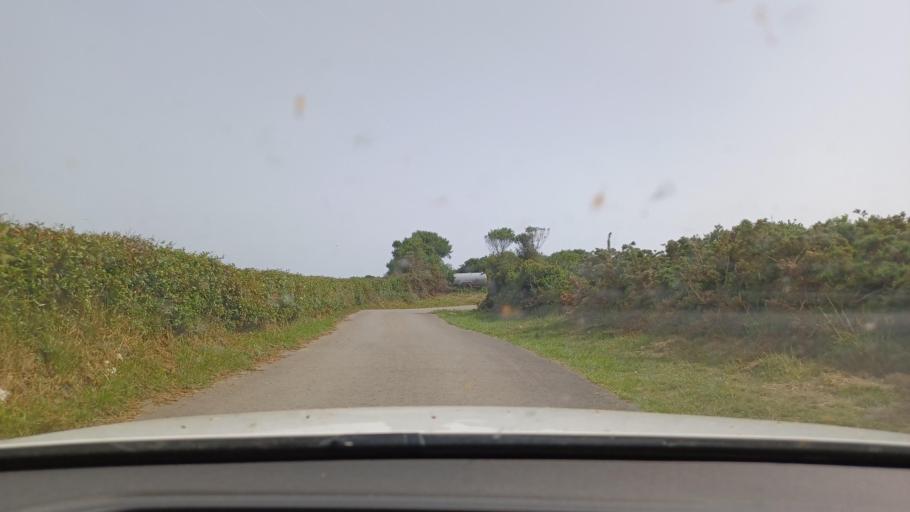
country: ES
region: Asturias
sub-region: Province of Asturias
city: Ribadesella
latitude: 43.4590
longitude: -5.0322
